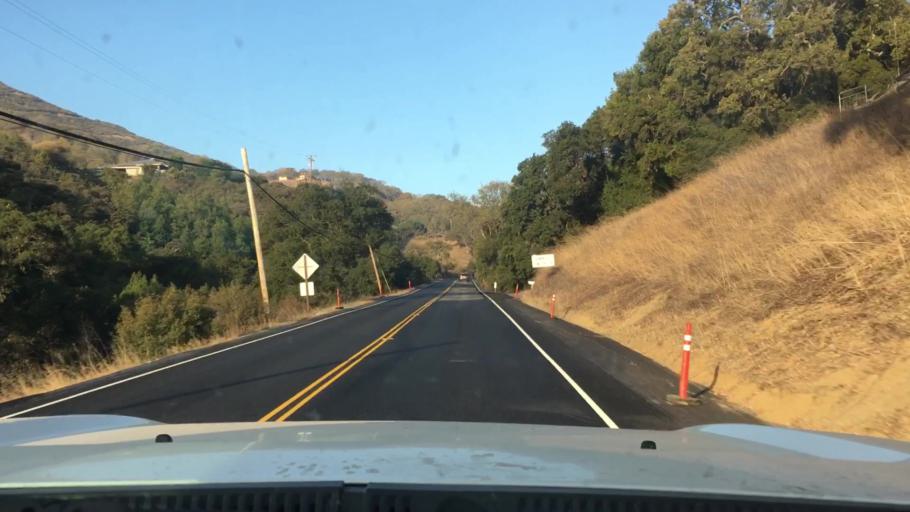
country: US
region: California
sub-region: San Luis Obispo County
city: Atascadero
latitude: 35.4512
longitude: -120.7048
